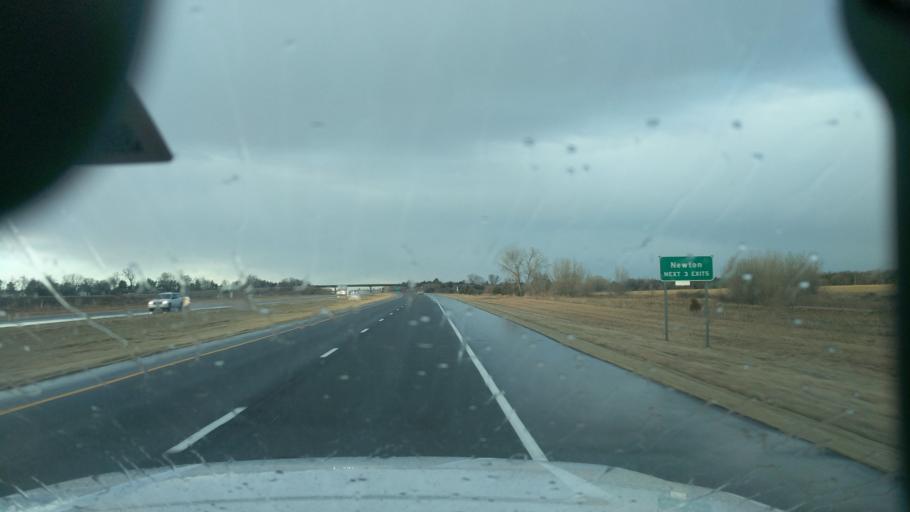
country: US
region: Kansas
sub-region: Harvey County
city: Newton
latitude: 37.9795
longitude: -97.3267
